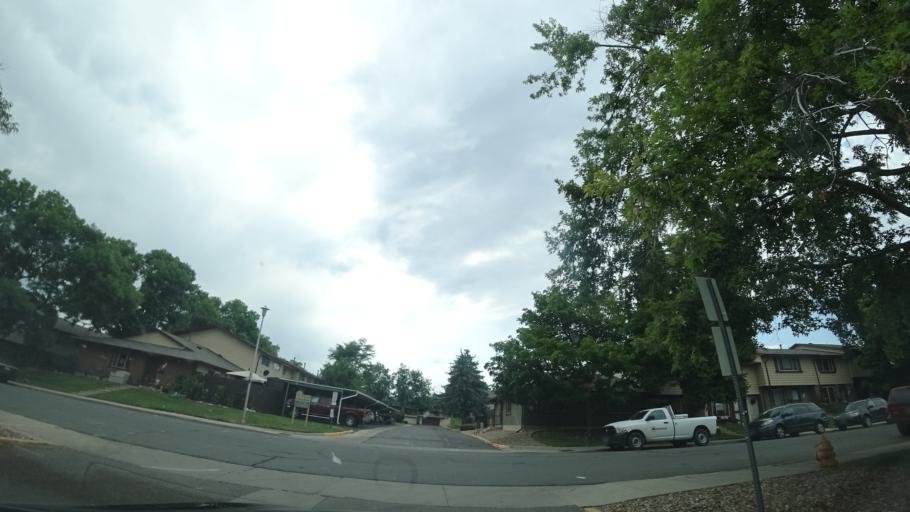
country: US
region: Colorado
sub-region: Jefferson County
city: Lakewood
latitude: 39.7087
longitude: -105.0886
